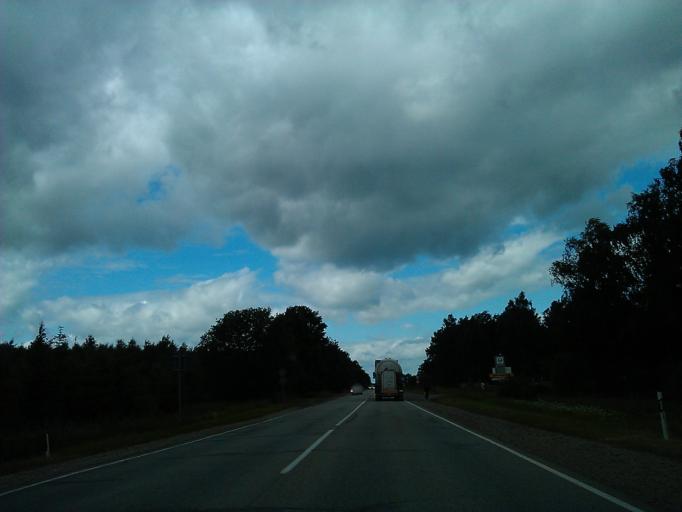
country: LV
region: Tukuma Rajons
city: Tukums
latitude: 56.9304
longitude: 23.2124
